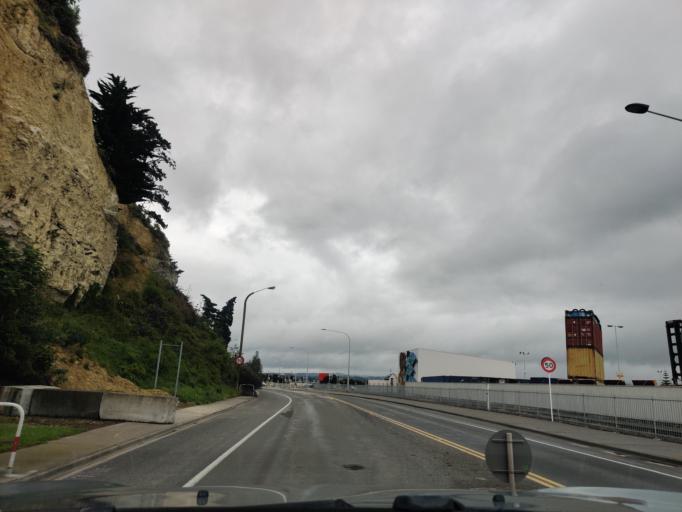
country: NZ
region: Hawke's Bay
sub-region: Napier City
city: Napier
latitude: -39.4776
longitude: 176.9132
